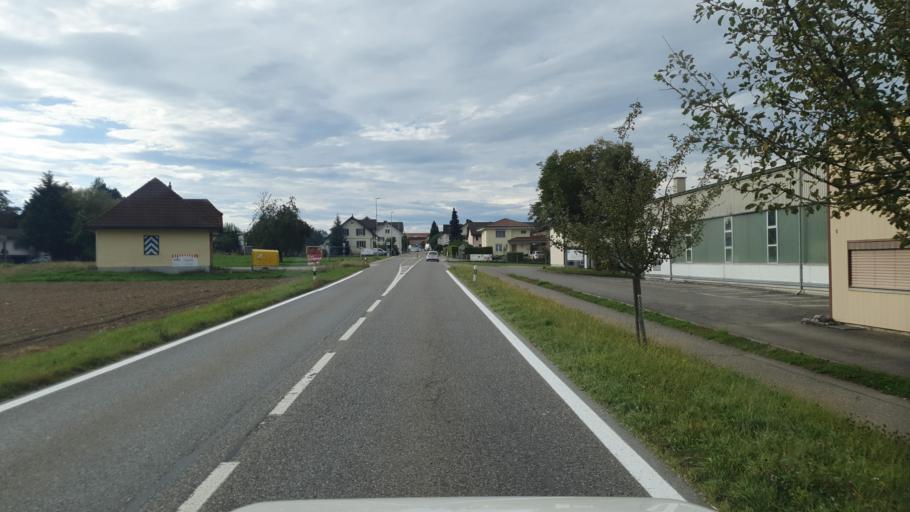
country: CH
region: Aargau
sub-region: Bezirk Bremgarten
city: Sarmenstorf
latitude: 47.2994
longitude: 8.2455
